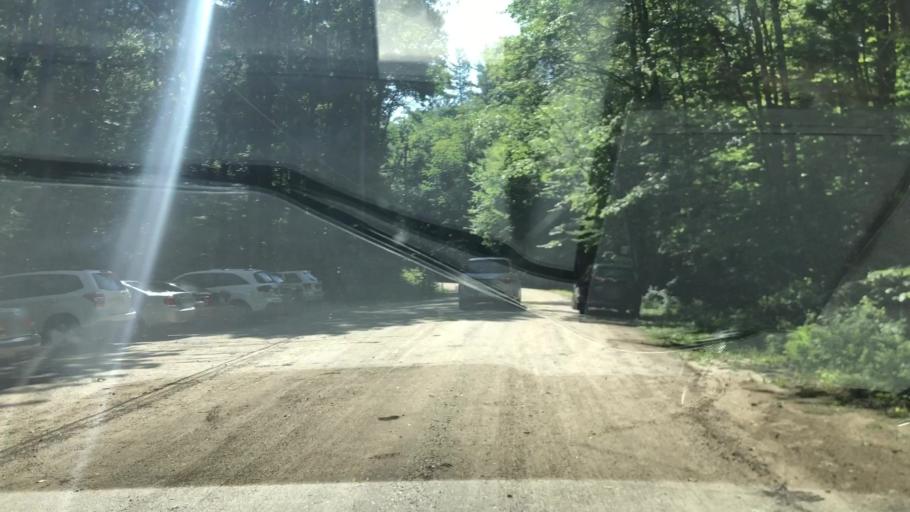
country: US
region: New Hampshire
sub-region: Hillsborough County
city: Mont Vernon
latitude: 42.9178
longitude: -71.6177
